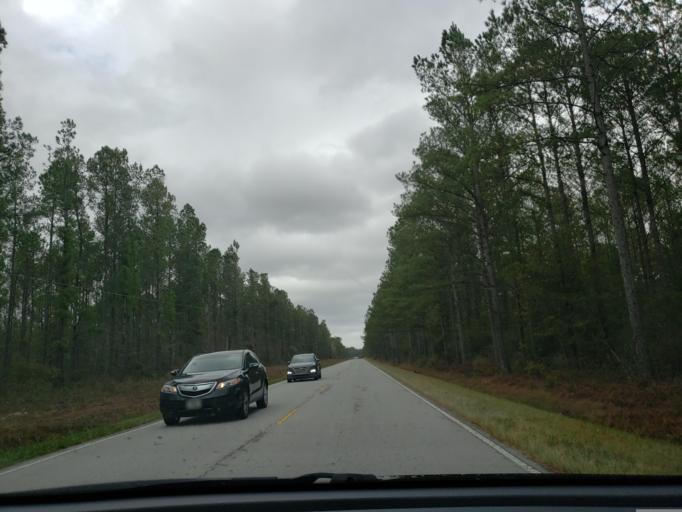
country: US
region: North Carolina
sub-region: Onslow County
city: Half Moon
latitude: 34.7275
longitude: -77.6014
